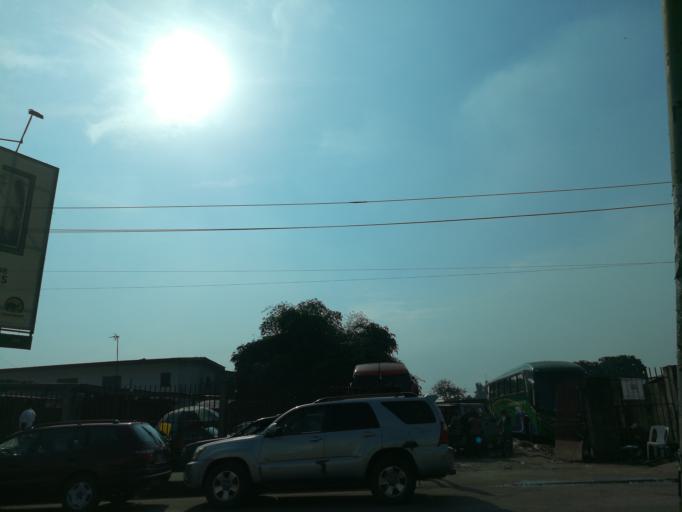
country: NG
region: Rivers
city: Port Harcourt
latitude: 4.8154
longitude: 7.0051
